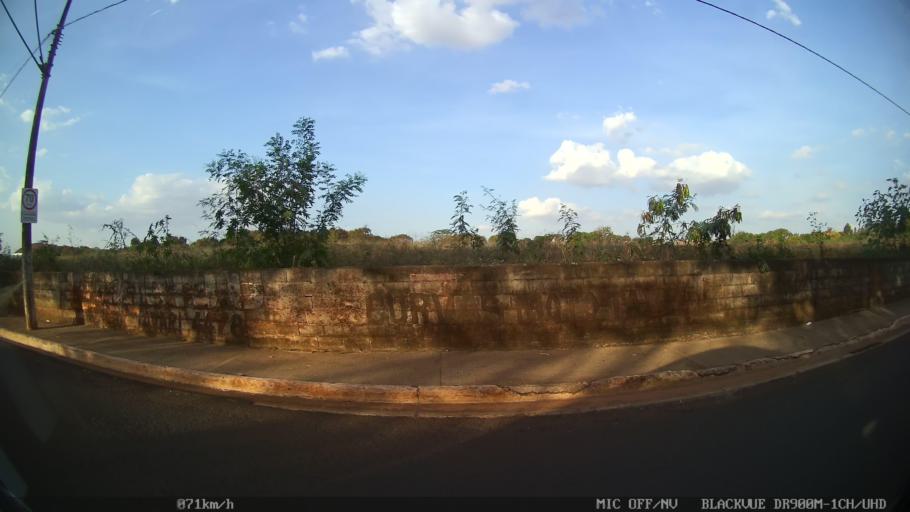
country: BR
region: Sao Paulo
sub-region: Ribeirao Preto
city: Ribeirao Preto
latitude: -21.1353
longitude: -47.8034
